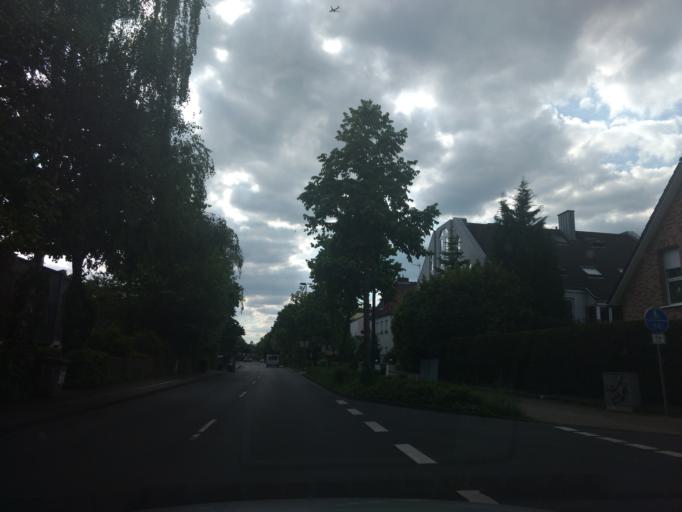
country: DE
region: North Rhine-Westphalia
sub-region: Regierungsbezirk Dusseldorf
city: Meerbusch
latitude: 51.2539
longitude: 6.7095
